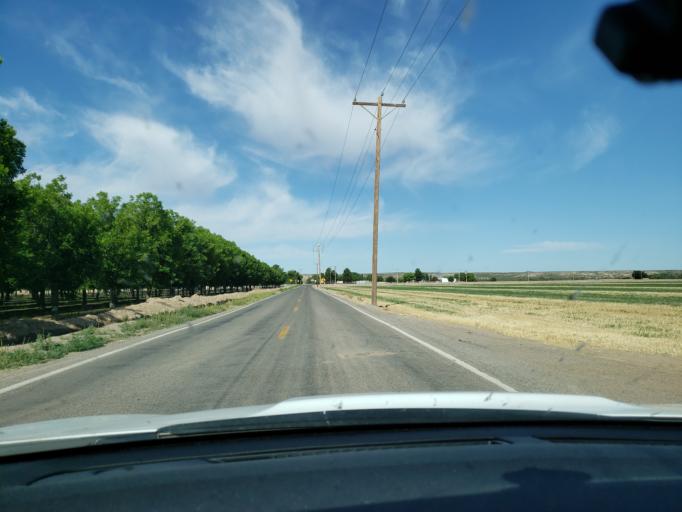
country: US
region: New Mexico
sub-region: Dona Ana County
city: Vado
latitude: 32.0624
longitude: -106.6739
